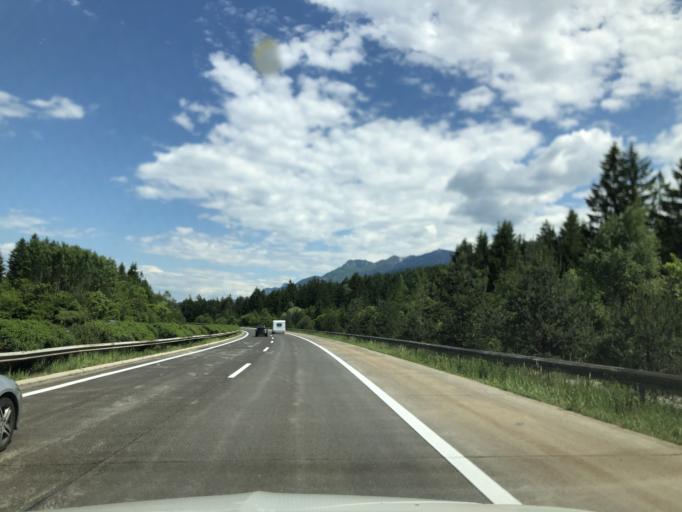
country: AT
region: Carinthia
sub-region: Politischer Bezirk Villach Land
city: Arnoldstein
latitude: 46.5578
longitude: 13.7509
